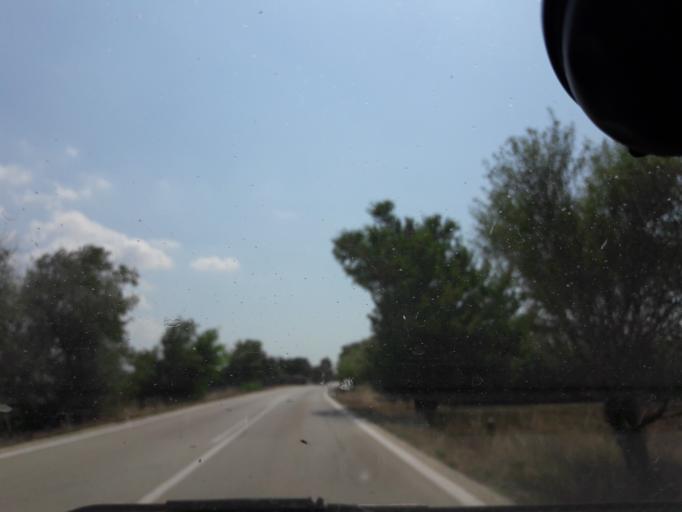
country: GR
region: North Aegean
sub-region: Nomos Lesvou
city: Myrina
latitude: 39.9324
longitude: 25.3408
